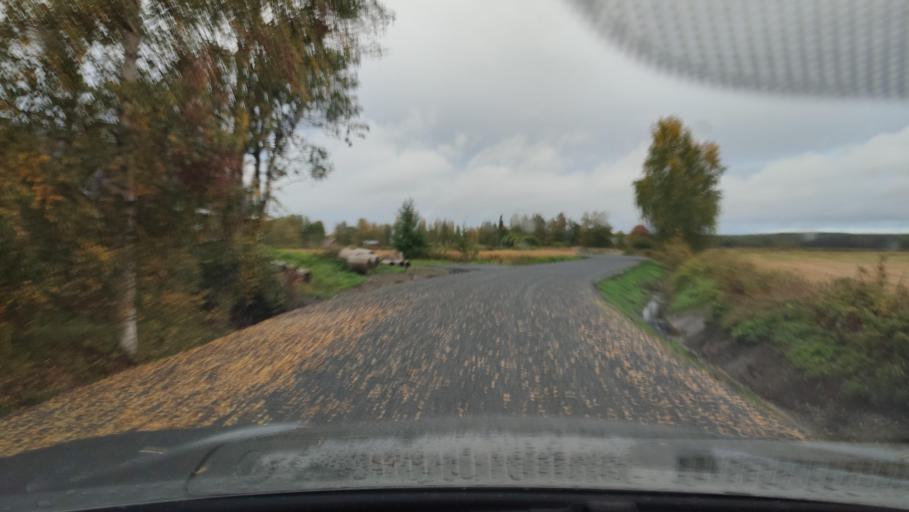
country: FI
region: Southern Ostrobothnia
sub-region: Suupohja
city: Karijoki
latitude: 62.2274
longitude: 21.6252
